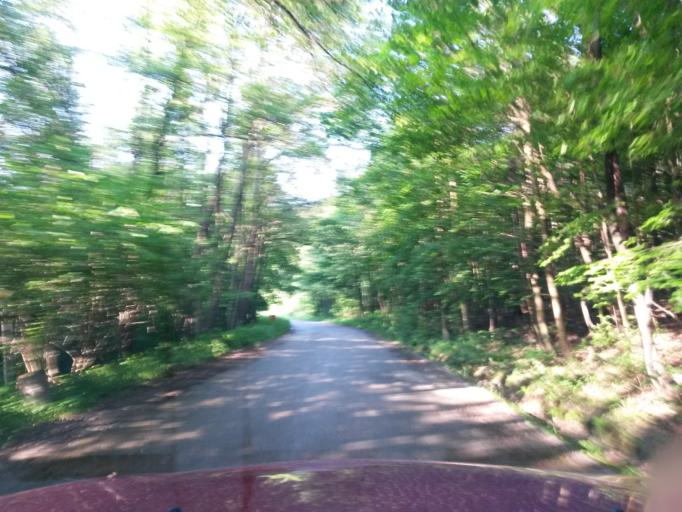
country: SK
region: Kosicky
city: Moldava nad Bodvou
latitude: 48.7452
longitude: 21.0259
